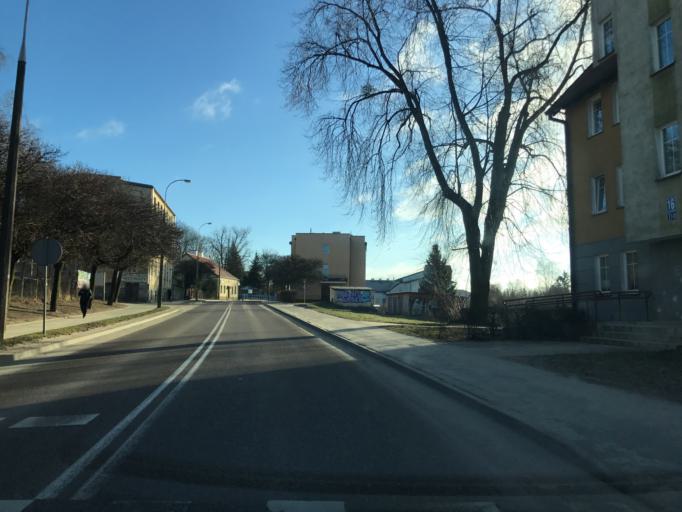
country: PL
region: Warmian-Masurian Voivodeship
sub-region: Powiat ostrodzki
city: Ostroda
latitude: 53.7043
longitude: 19.9637
